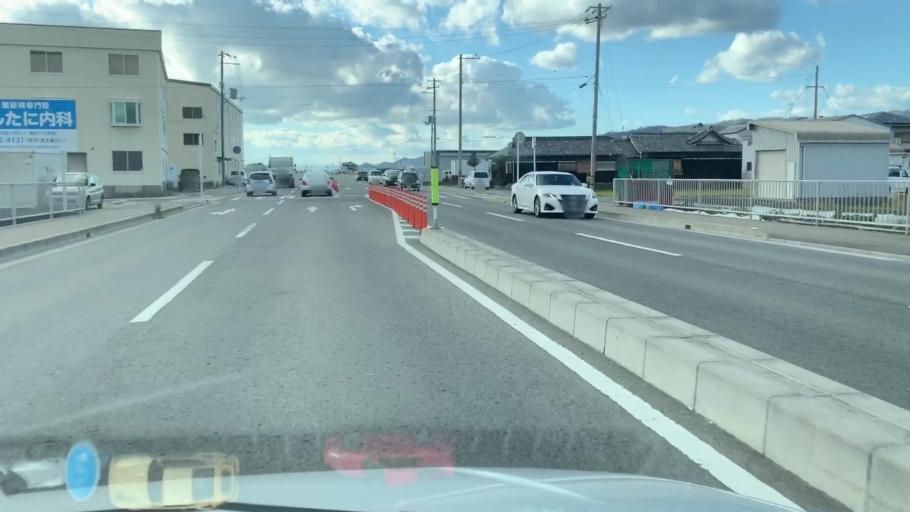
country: JP
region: Wakayama
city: Iwade
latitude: 34.2624
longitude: 135.2472
